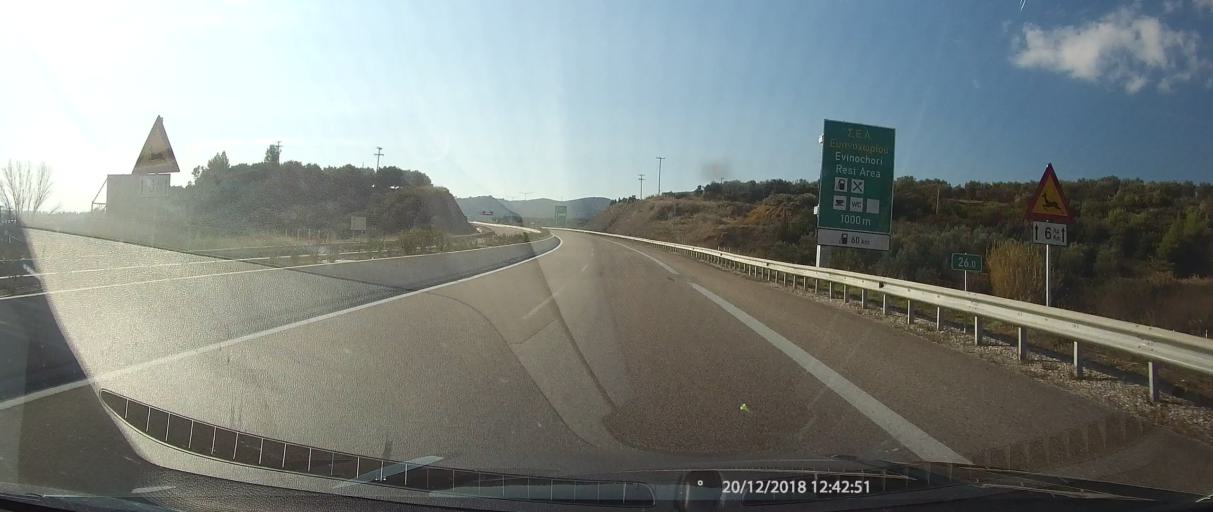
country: GR
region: West Greece
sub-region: Nomos Aitolias kai Akarnanias
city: Galatas
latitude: 38.3959
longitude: 21.5559
